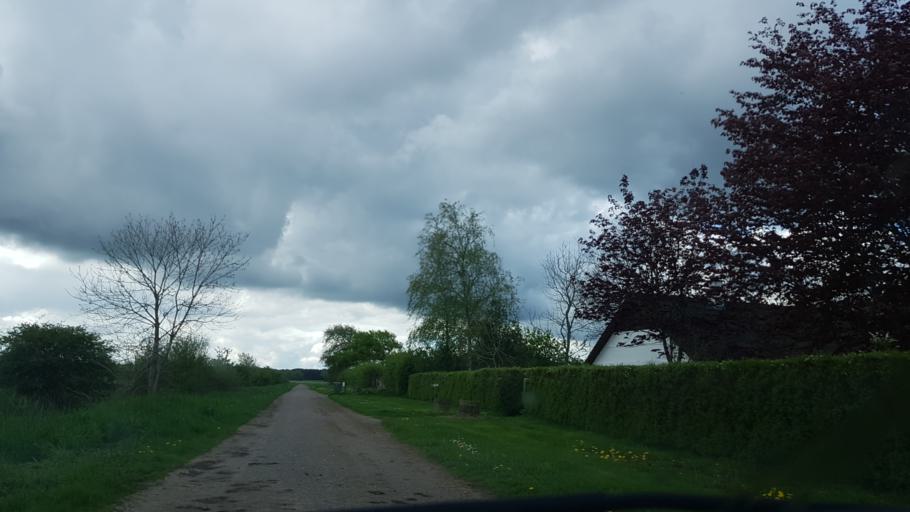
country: DK
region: South Denmark
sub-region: Haderslev Kommune
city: Vojens
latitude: 55.2430
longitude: 9.1952
